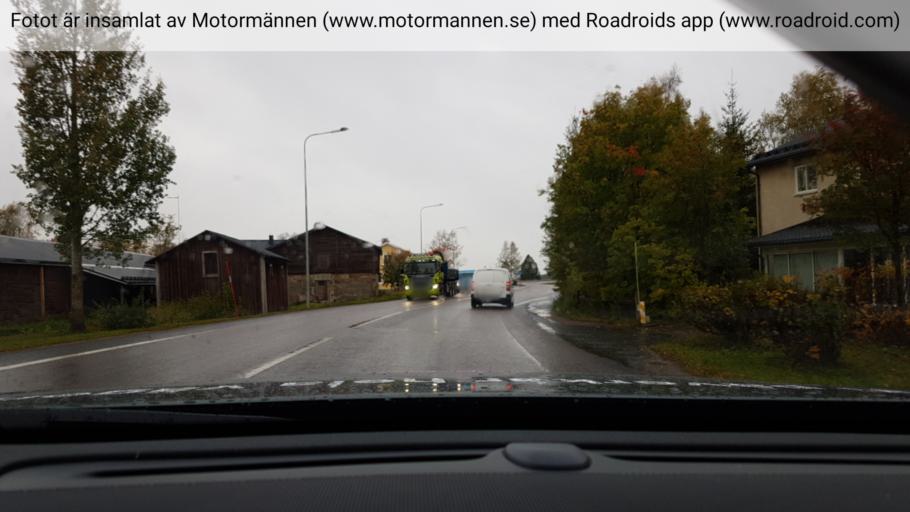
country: SE
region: Norrbotten
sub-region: Lulea Kommun
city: Gammelstad
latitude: 65.5854
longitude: 22.0298
